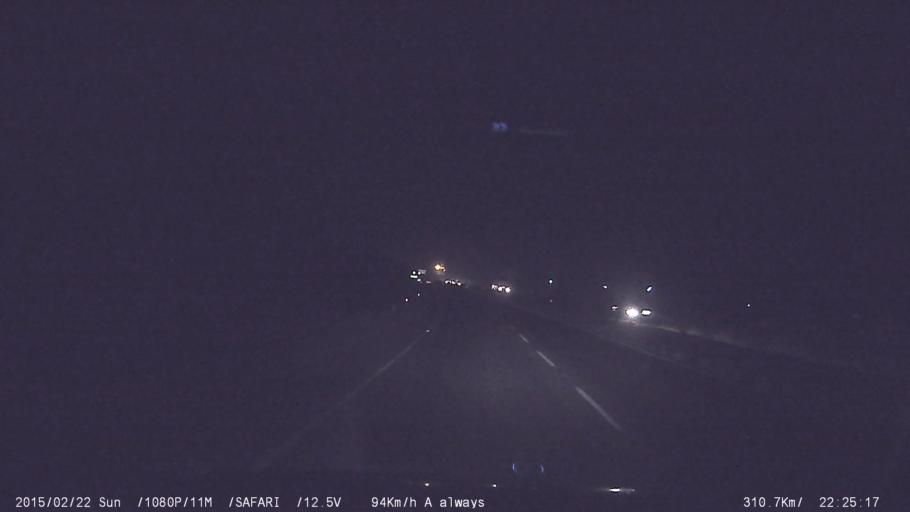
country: IN
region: Tamil Nadu
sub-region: Namakkal
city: Velur
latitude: 11.0469
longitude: 78.0556
